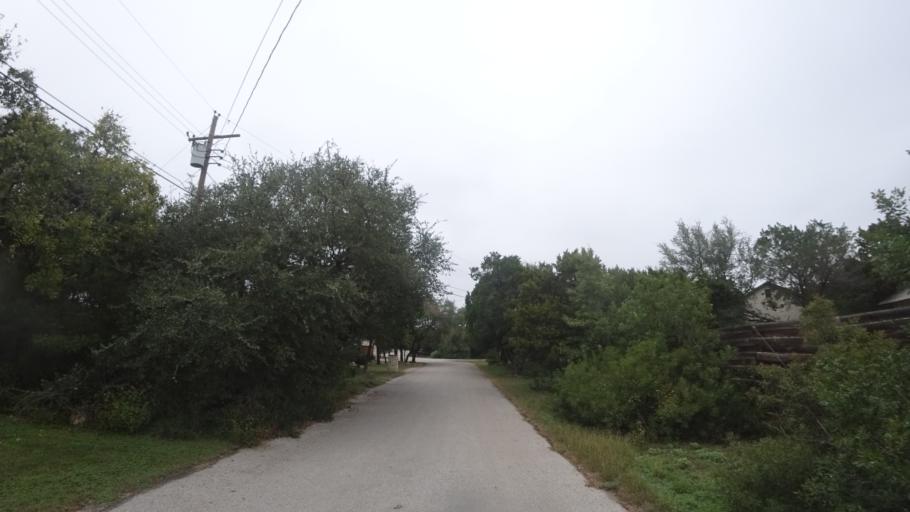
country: US
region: Texas
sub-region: Travis County
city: Hudson Bend
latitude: 30.3938
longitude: -97.9192
